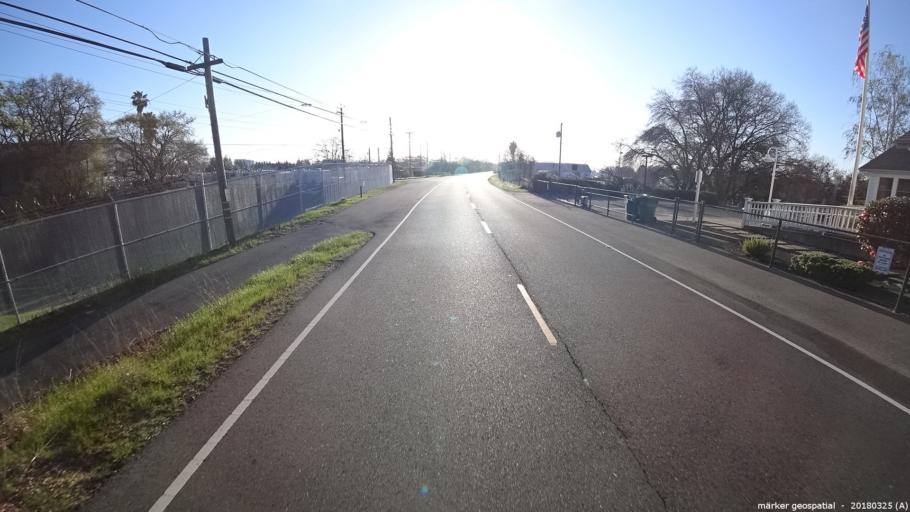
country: US
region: California
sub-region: Yolo County
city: West Sacramento
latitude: 38.6055
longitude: -121.5248
